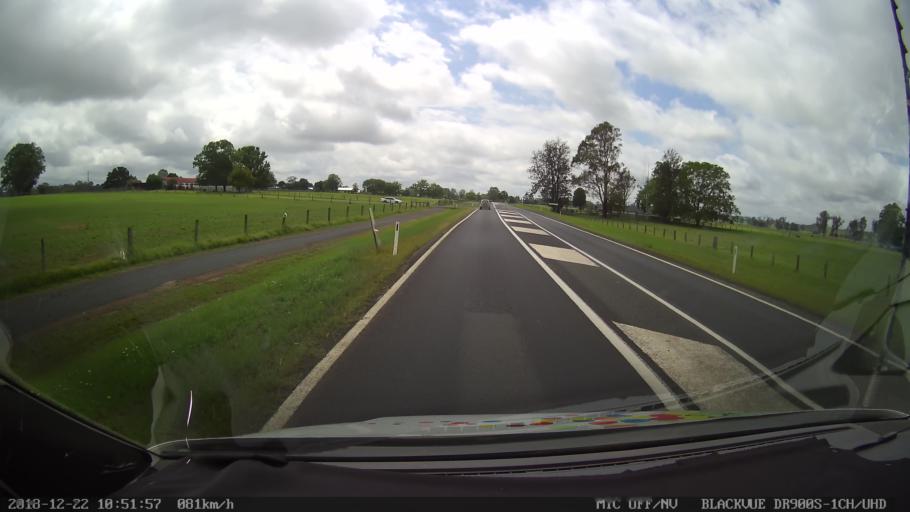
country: AU
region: New South Wales
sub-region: Clarence Valley
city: South Grafton
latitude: -29.6904
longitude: 152.9033
